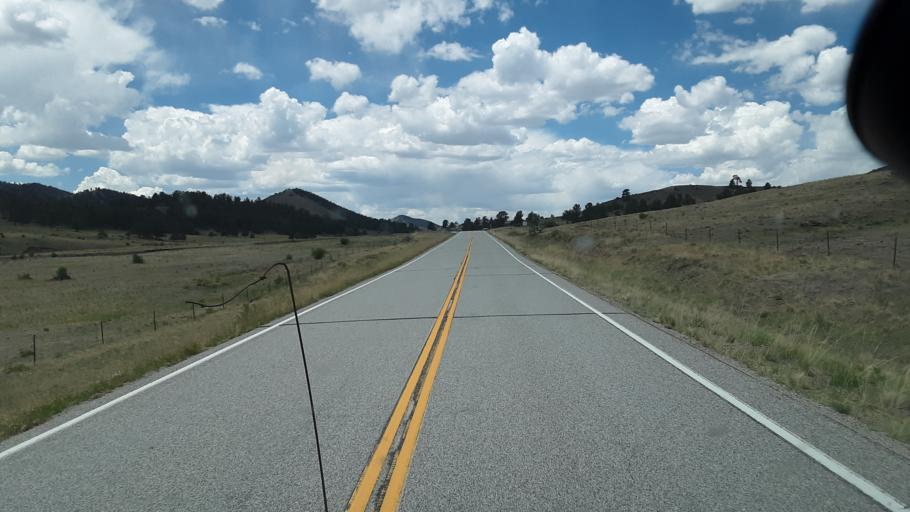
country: US
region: Colorado
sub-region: Teller County
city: Cripple Creek
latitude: 38.7905
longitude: -105.5882
